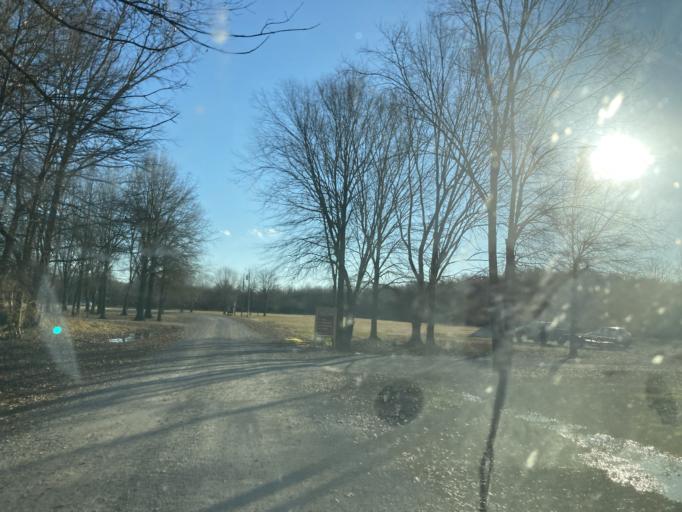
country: US
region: Mississippi
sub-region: Yazoo County
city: Yazoo City
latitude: 32.9239
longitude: -90.5744
